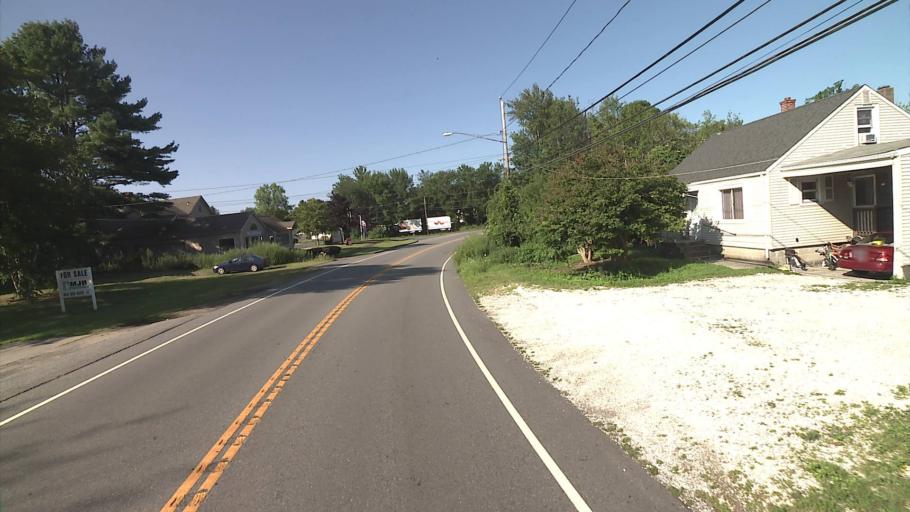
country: US
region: Connecticut
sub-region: Middlesex County
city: Westbrook Center
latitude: 41.2808
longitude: -72.4239
